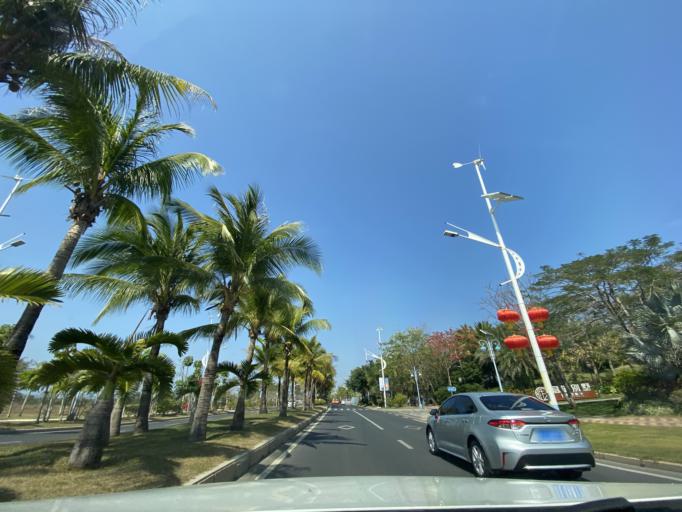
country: CN
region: Hainan
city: Haitangwan
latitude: 18.3469
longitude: 109.7332
